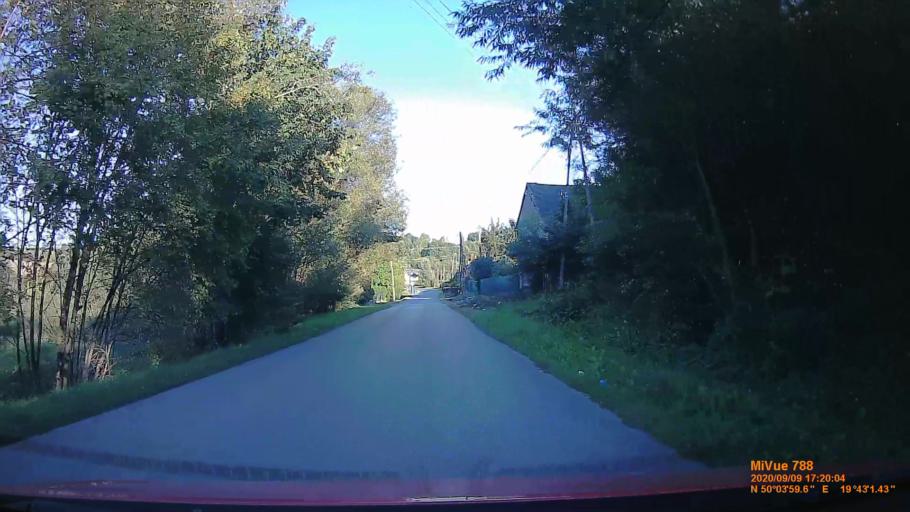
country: PL
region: Lesser Poland Voivodeship
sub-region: Powiat krakowski
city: Mnikow
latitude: 50.0666
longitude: 19.7171
